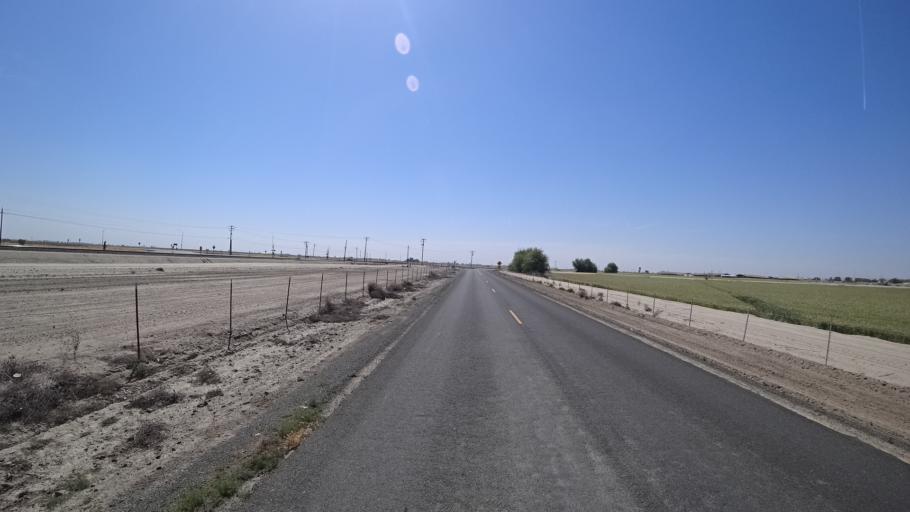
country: US
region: California
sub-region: Kings County
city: Corcoran
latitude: 36.0711
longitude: -119.5379
